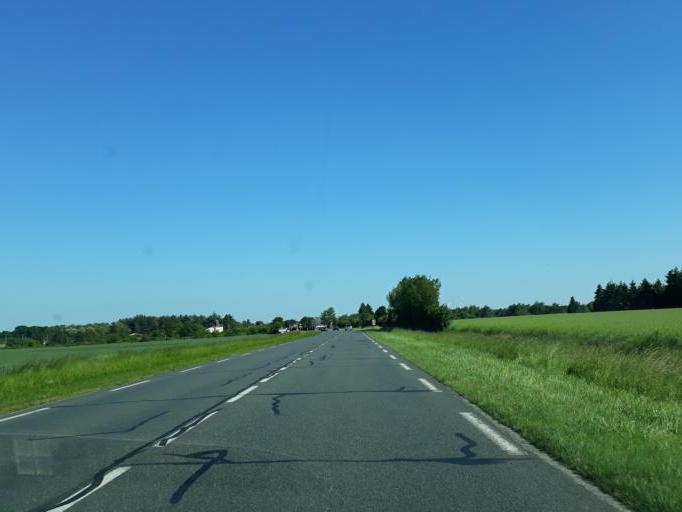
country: FR
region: Centre
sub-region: Departement du Loiret
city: Briare
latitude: 47.6005
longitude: 2.7866
